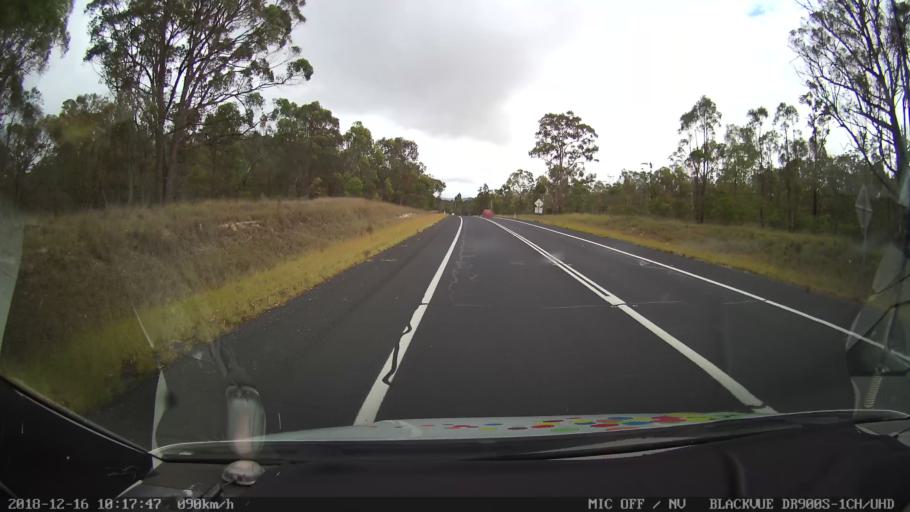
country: AU
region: New South Wales
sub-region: Tenterfield Municipality
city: Carrolls Creek
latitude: -29.2522
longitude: 151.9944
